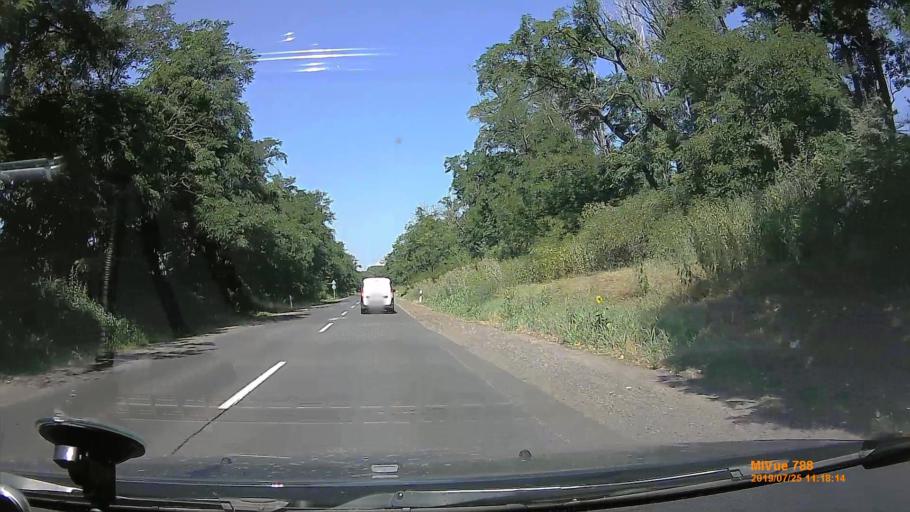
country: HU
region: Szabolcs-Szatmar-Bereg
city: Nagykallo
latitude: 47.8963
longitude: 21.7986
